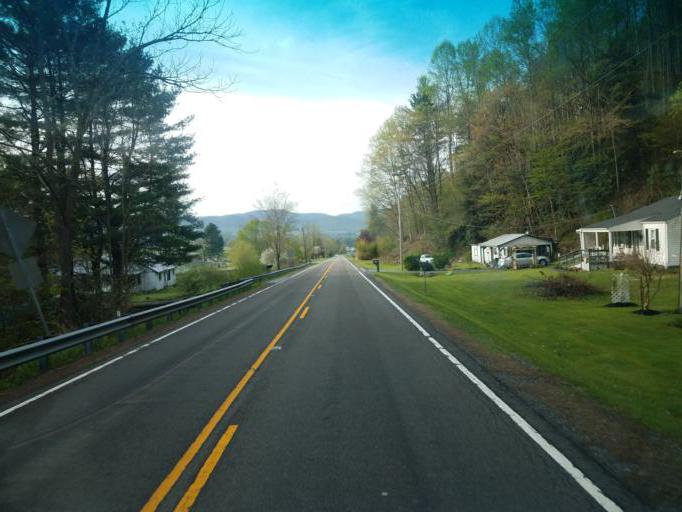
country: US
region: Virginia
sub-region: Smyth County
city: Atkins
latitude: 36.7977
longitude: -81.4026
